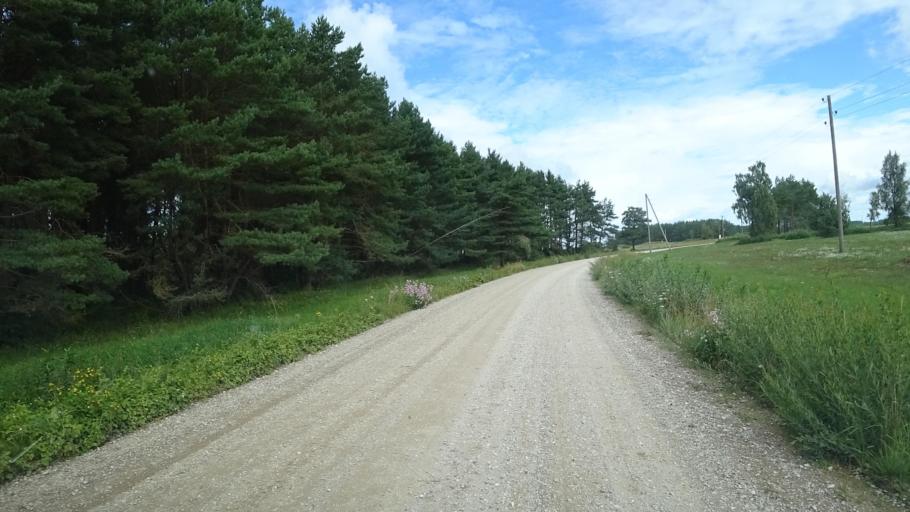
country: LV
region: Liepaja
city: Vec-Liepaja
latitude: 56.6407
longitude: 21.0447
